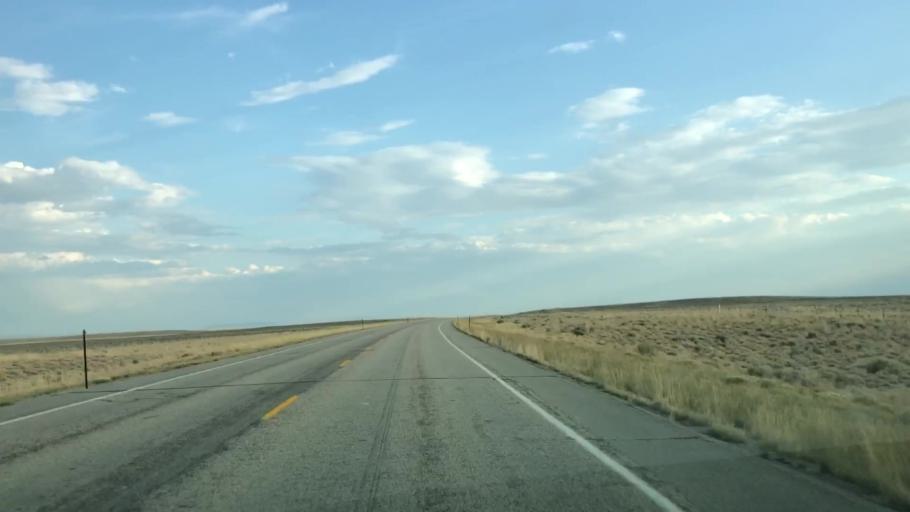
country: US
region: Wyoming
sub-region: Sweetwater County
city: North Rock Springs
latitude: 42.2539
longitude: -109.4680
